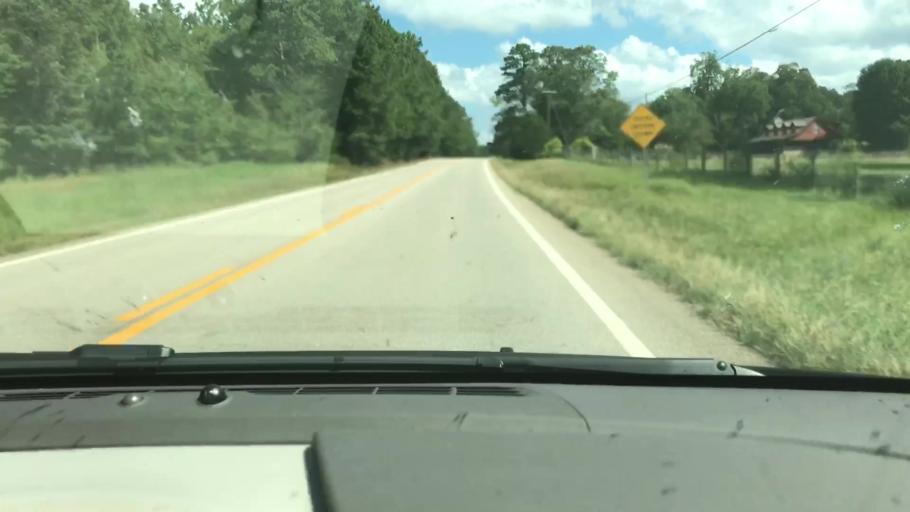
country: US
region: Georgia
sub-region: Troup County
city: La Grange
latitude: 32.9366
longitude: -85.0192
